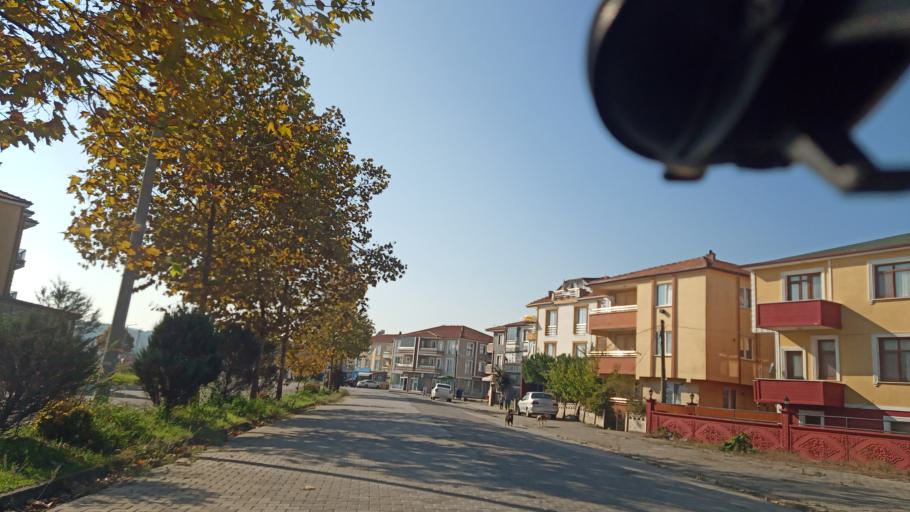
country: TR
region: Sakarya
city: Karasu
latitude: 41.0895
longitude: 30.7414
